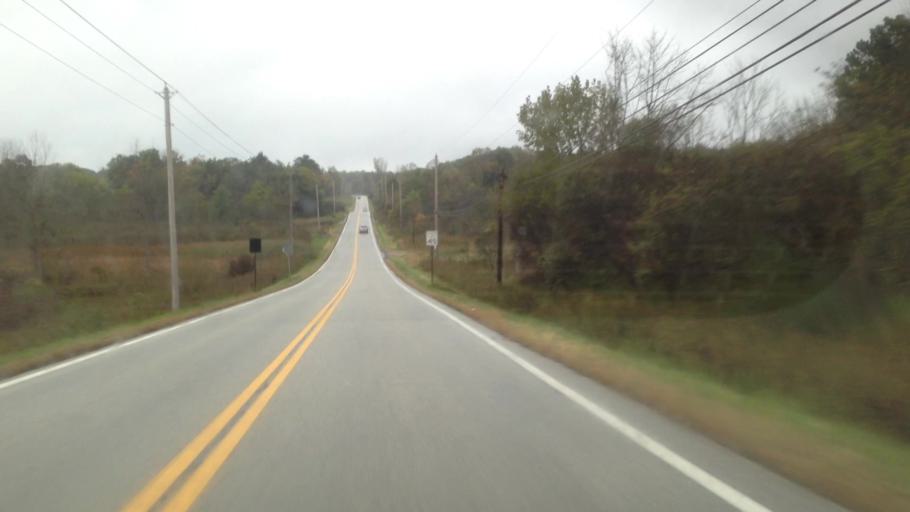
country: US
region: Ohio
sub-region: Summit County
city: Hudson
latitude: 41.2602
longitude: -81.4718
